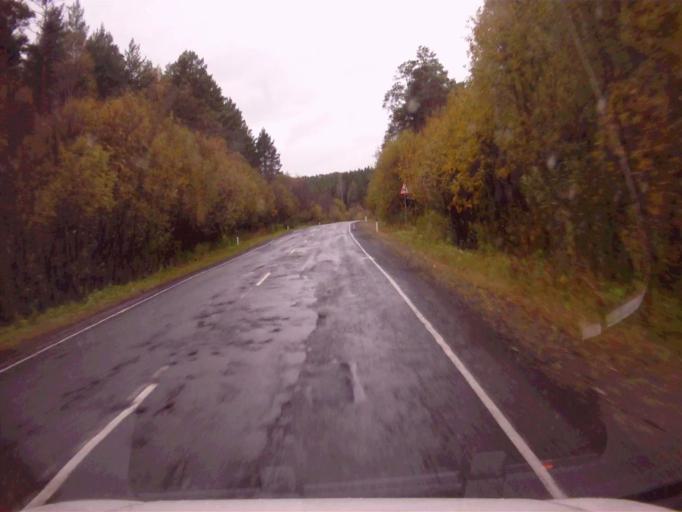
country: RU
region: Chelyabinsk
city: Verkhniy Ufaley
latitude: 56.0493
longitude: 60.1403
